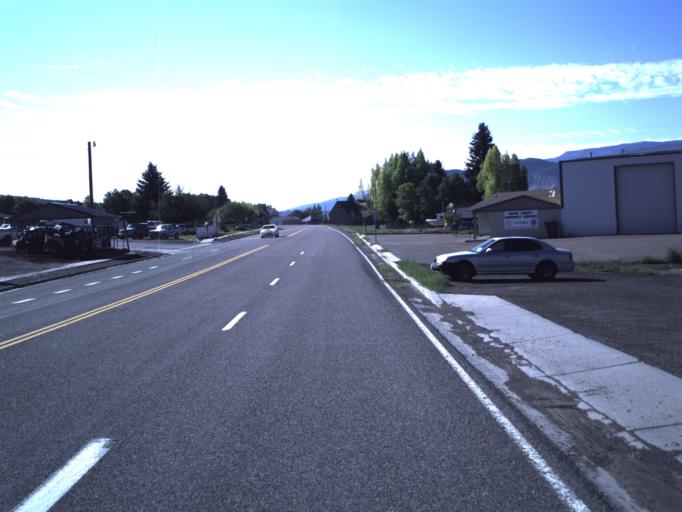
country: US
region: Utah
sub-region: Wayne County
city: Loa
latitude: 38.3426
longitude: -111.5530
